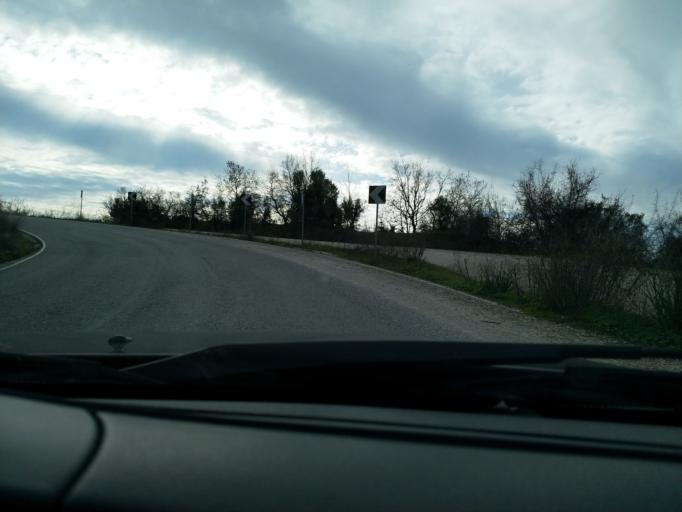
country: GR
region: Epirus
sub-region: Nomos Prevezis
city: Filippiada
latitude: 39.2235
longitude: 20.8430
